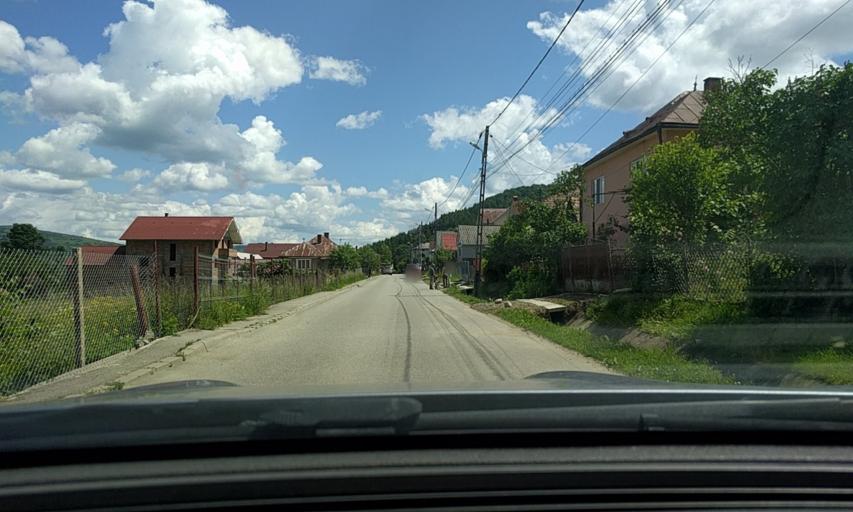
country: RO
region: Bistrita-Nasaud
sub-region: Oras Nasaud
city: Nasaud
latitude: 47.2770
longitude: 24.4166
